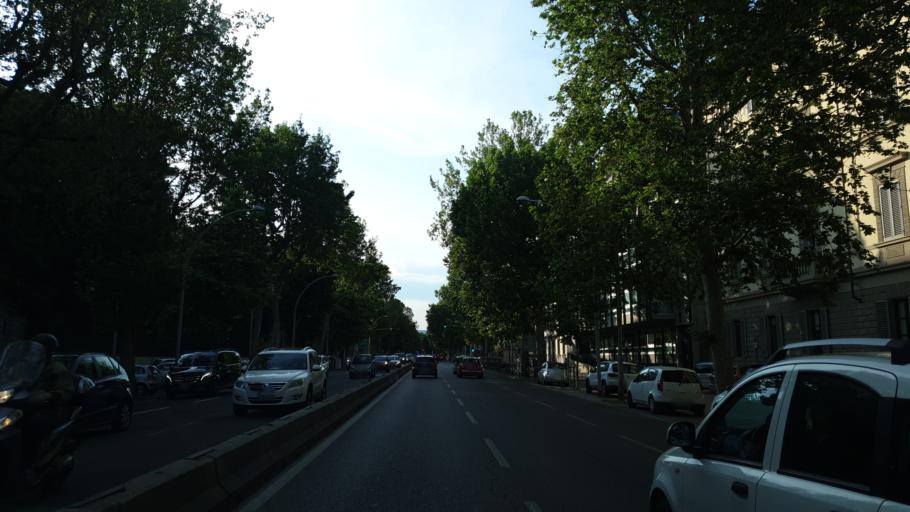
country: IT
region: Tuscany
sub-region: Province of Florence
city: Florence
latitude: 43.7793
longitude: 11.2663
